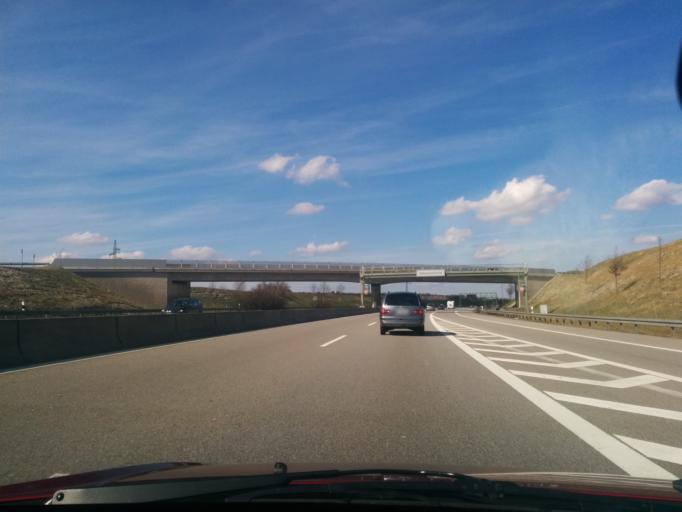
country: DE
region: Bavaria
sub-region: Upper Bavaria
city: Germering
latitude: 48.1485
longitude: 11.3943
